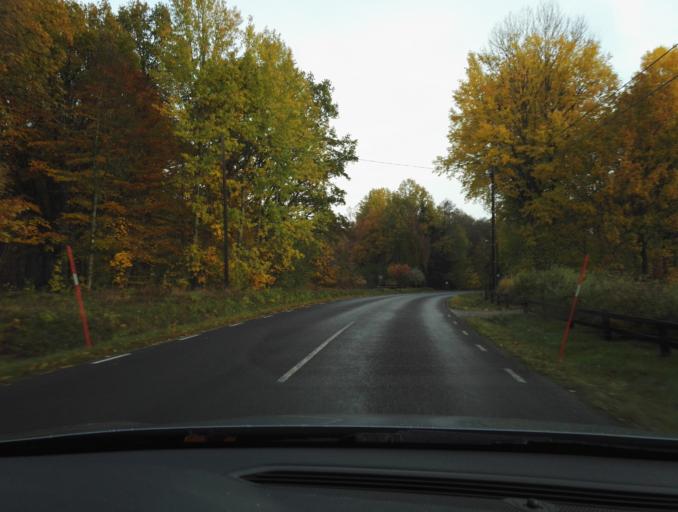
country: SE
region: Kronoberg
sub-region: Alvesta Kommun
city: Moheda
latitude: 57.0007
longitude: 14.6771
